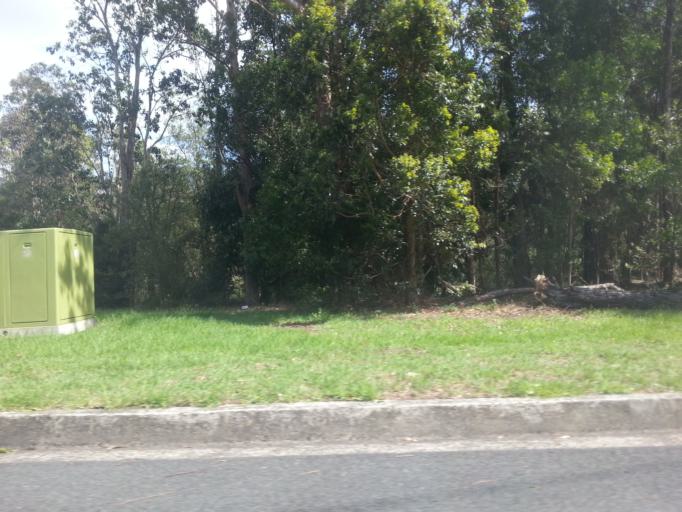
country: AU
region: New South Wales
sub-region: Wollongong
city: Keiraville
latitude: -34.4216
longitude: 150.8748
